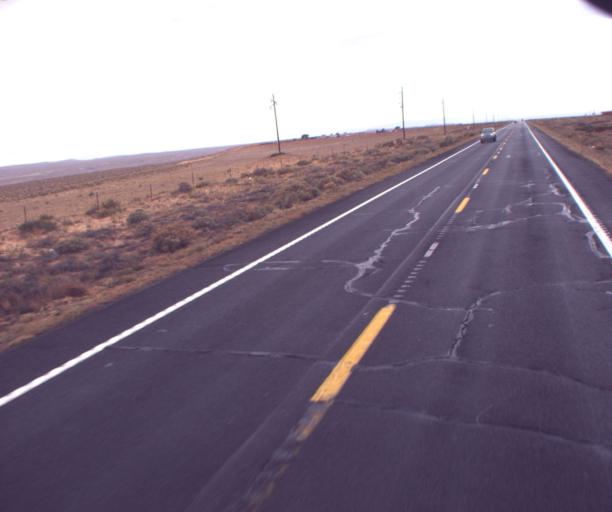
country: US
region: Arizona
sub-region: Coconino County
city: Tuba City
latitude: 36.1485
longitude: -111.1398
